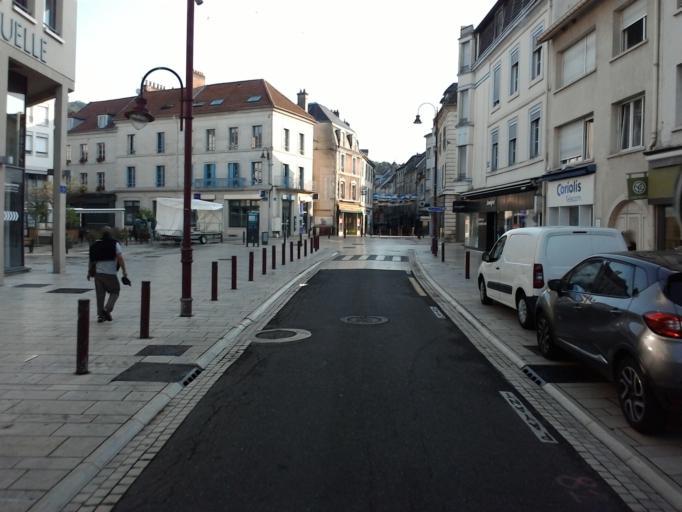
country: FR
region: Franche-Comte
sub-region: Departement de la Haute-Saone
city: Navenne
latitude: 47.6214
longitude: 6.1554
